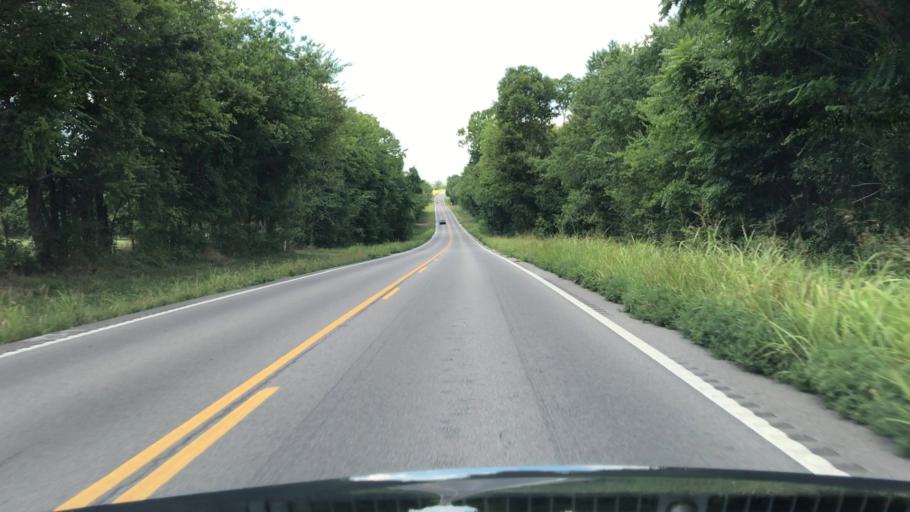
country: US
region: Tennessee
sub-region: Williamson County
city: Nolensville
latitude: 35.8524
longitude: -86.6403
